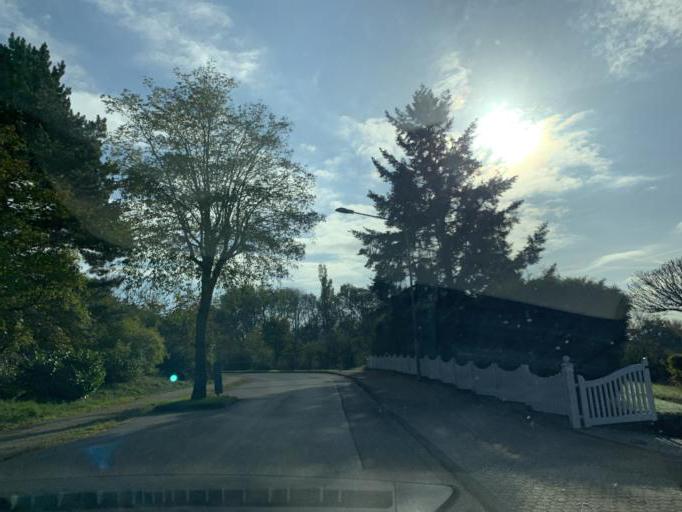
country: DE
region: North Rhine-Westphalia
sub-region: Regierungsbezirk Koln
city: Dueren
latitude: 50.8207
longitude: 6.4786
